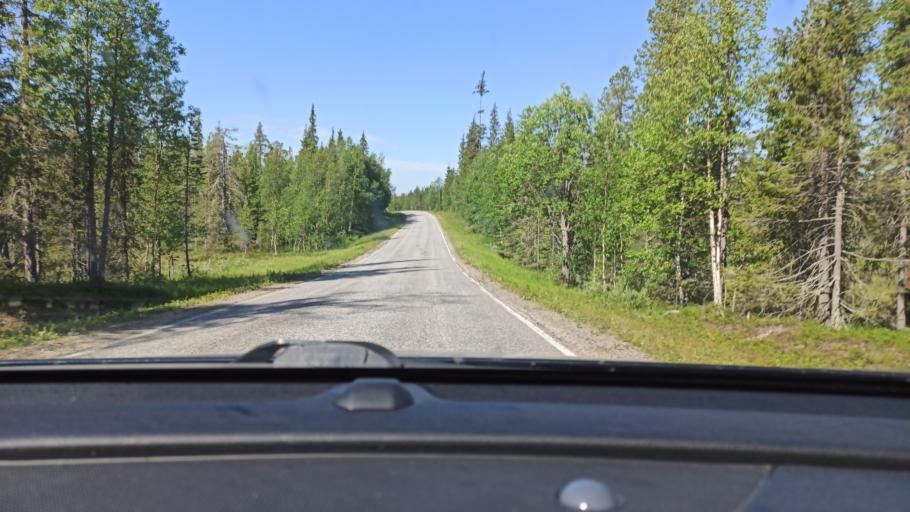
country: FI
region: Lapland
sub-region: Tunturi-Lappi
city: Kolari
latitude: 67.6834
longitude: 24.1270
